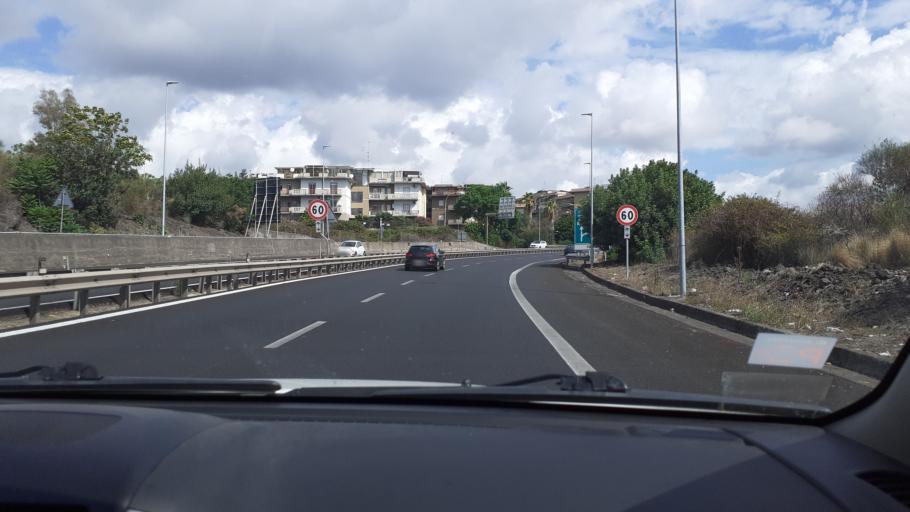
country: IT
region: Sicily
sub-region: Catania
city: Canalicchio
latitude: 37.5324
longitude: 15.0948
